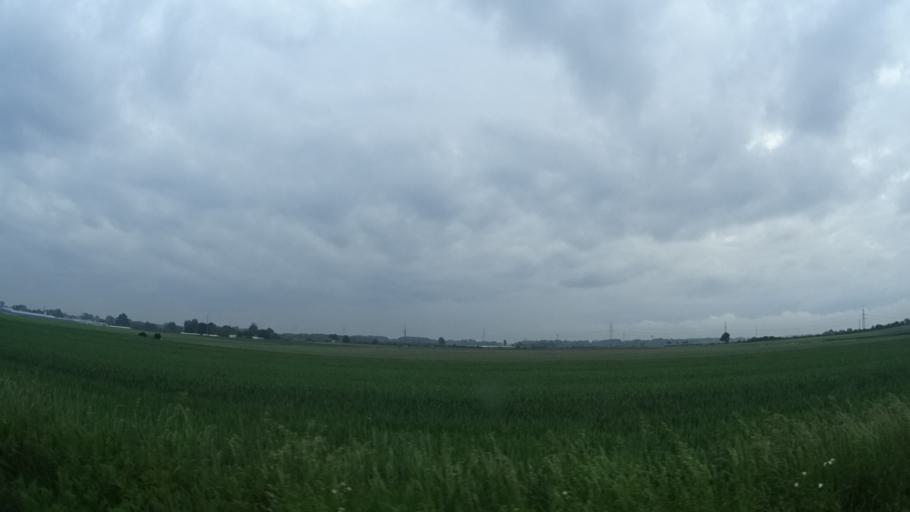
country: DE
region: Rheinland-Pfalz
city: Rulzheim
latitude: 49.1790
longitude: 8.2861
